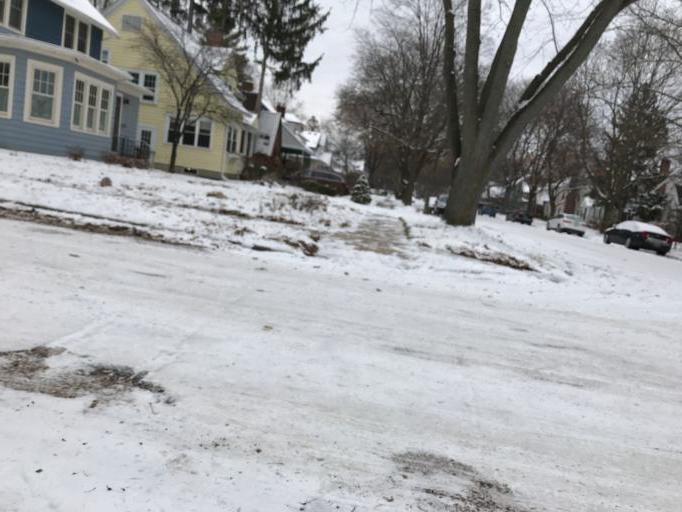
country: US
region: Michigan
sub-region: Washtenaw County
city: Ann Arbor
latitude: 42.2616
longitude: -83.7351
